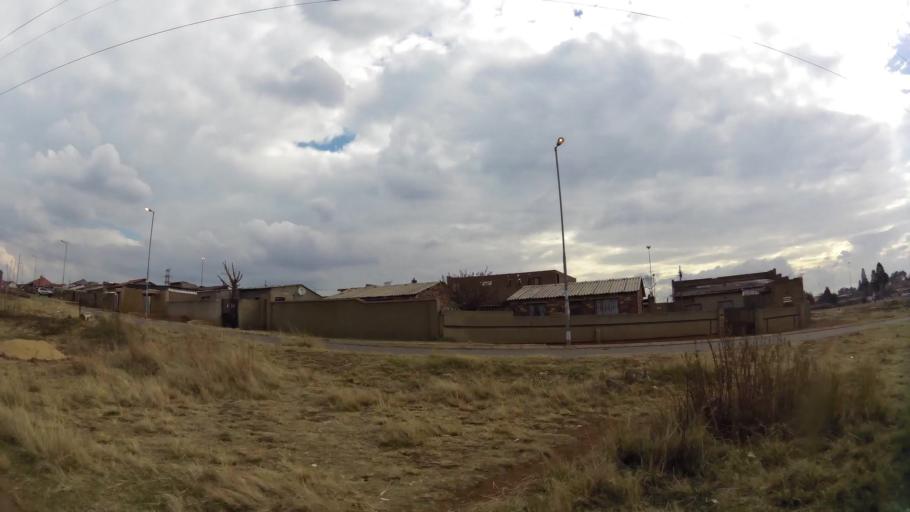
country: ZA
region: Gauteng
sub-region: City of Johannesburg Metropolitan Municipality
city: Soweto
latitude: -26.2415
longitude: 27.8591
